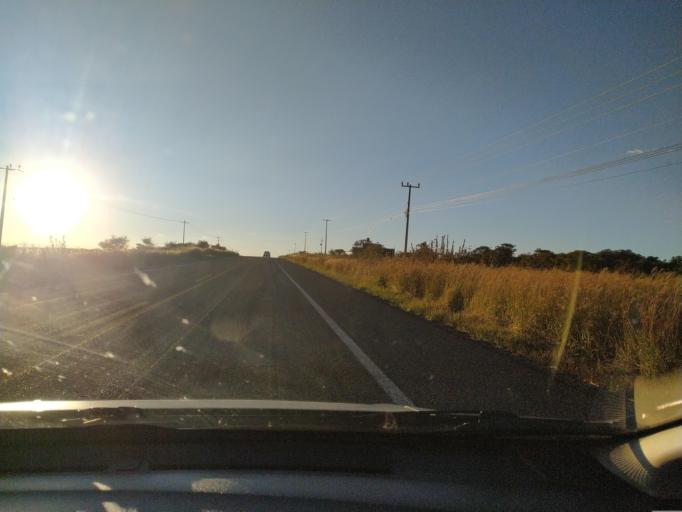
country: MX
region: Jalisco
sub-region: San Julian
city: Colonia Veintitres de Mayo
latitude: 21.0111
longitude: -102.2198
